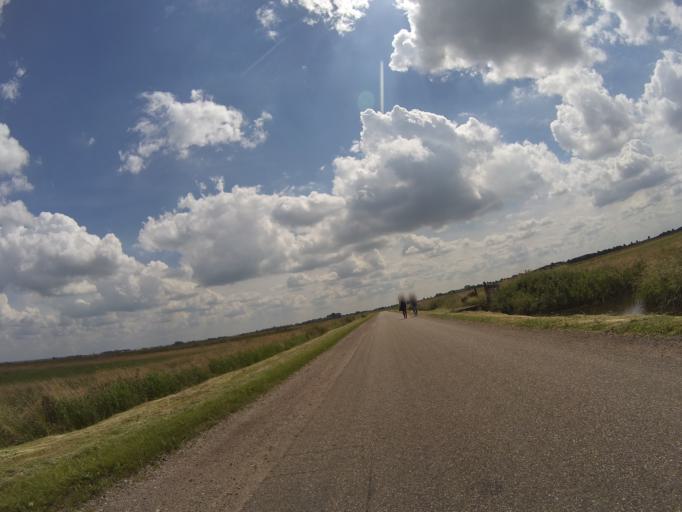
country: NL
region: Utrecht
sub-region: Gemeente Bunschoten
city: Bunschoten
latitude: 52.2358
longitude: 5.4129
